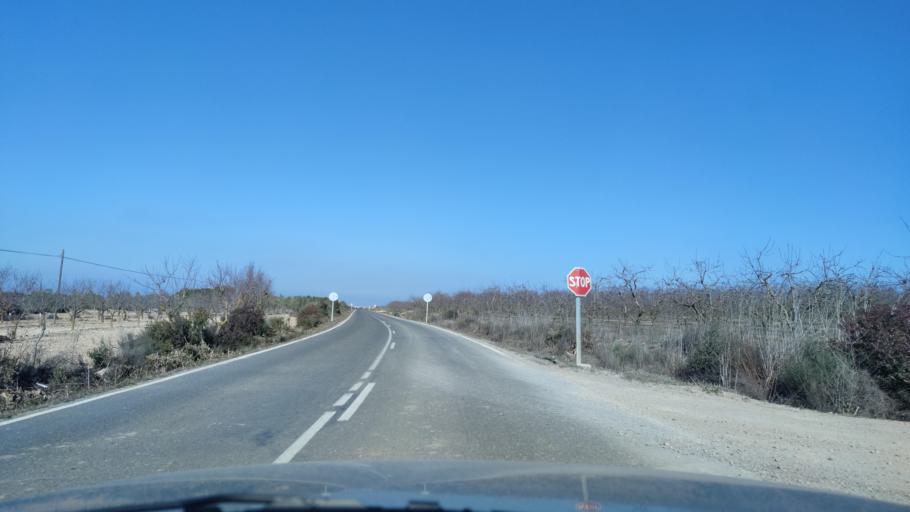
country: ES
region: Catalonia
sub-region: Provincia de Lleida
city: Maials
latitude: 41.3458
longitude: 0.4691
